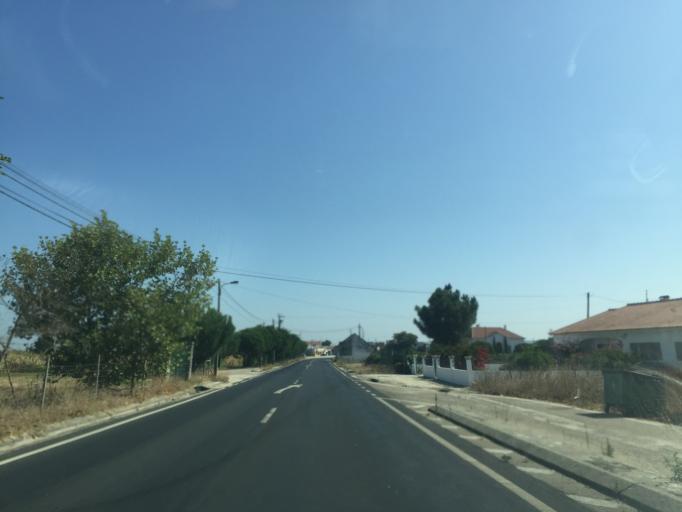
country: PT
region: Santarem
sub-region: Alpiarca
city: Alpiarca
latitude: 39.2725
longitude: -8.5647
